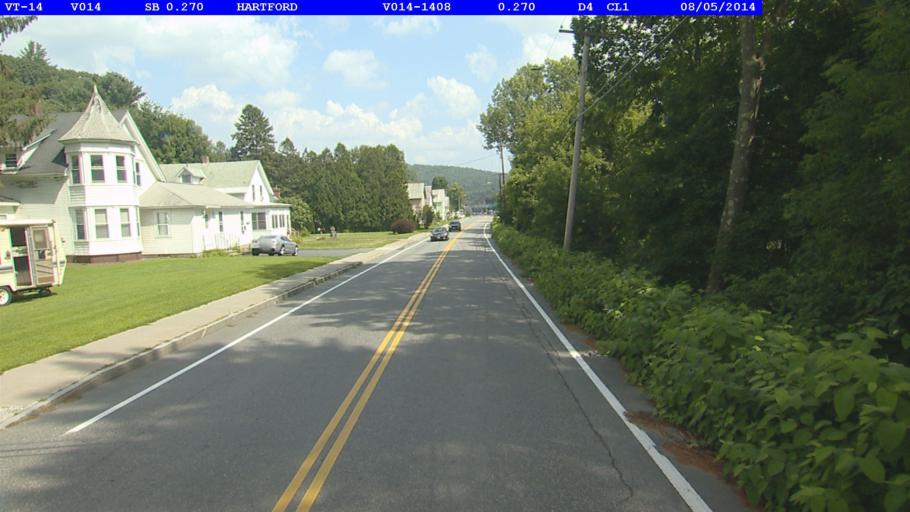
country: US
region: Vermont
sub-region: Windsor County
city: White River Junction
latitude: 43.6537
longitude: -72.3242
